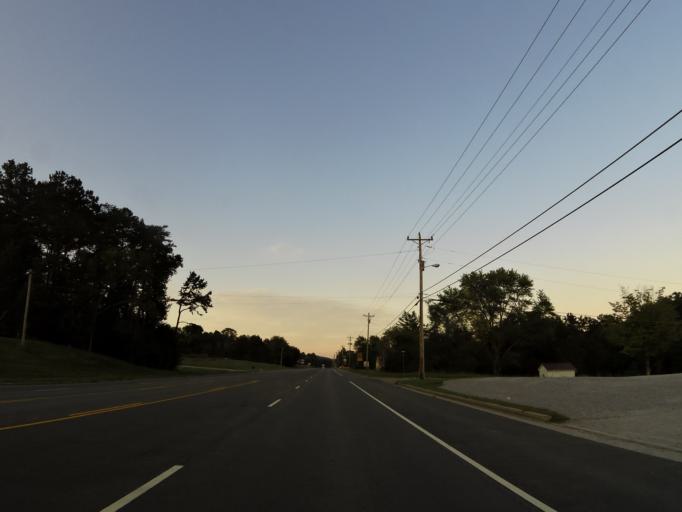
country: US
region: Tennessee
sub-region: Roane County
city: Kingston
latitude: 35.8894
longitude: -84.4183
